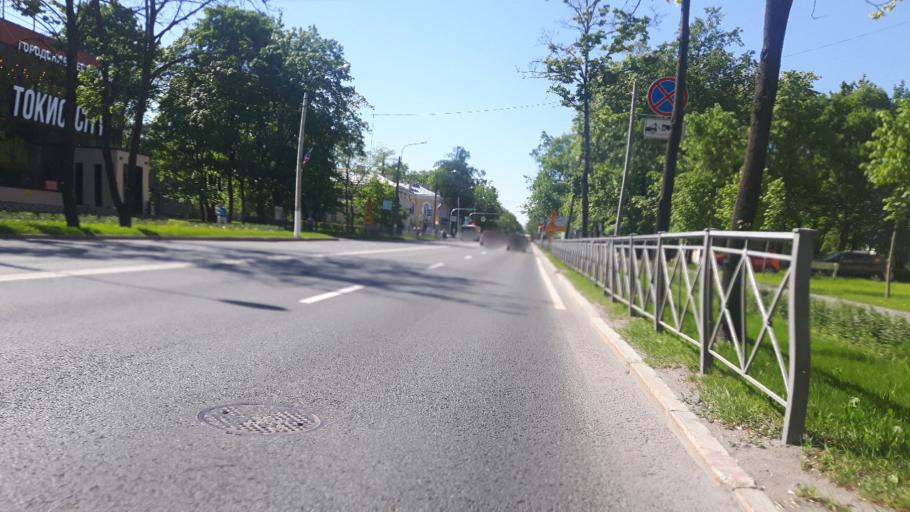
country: RU
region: St.-Petersburg
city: Peterhof
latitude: 59.8777
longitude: 29.9260
